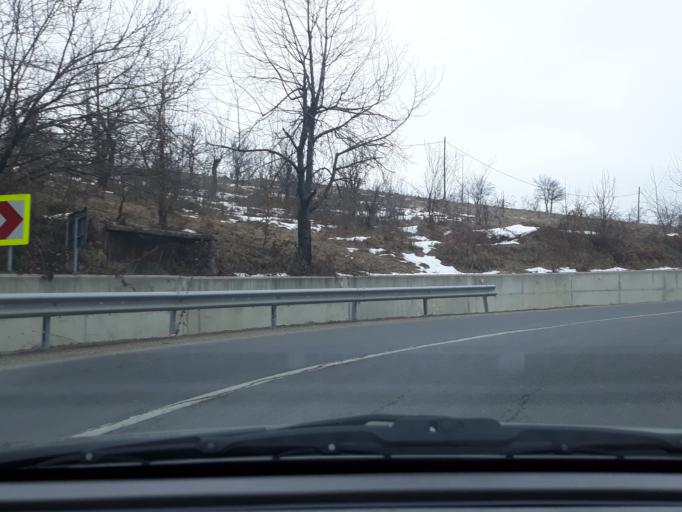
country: RO
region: Bihor
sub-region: Comuna Sinteu
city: Sinteu
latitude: 47.1222
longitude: 22.4608
